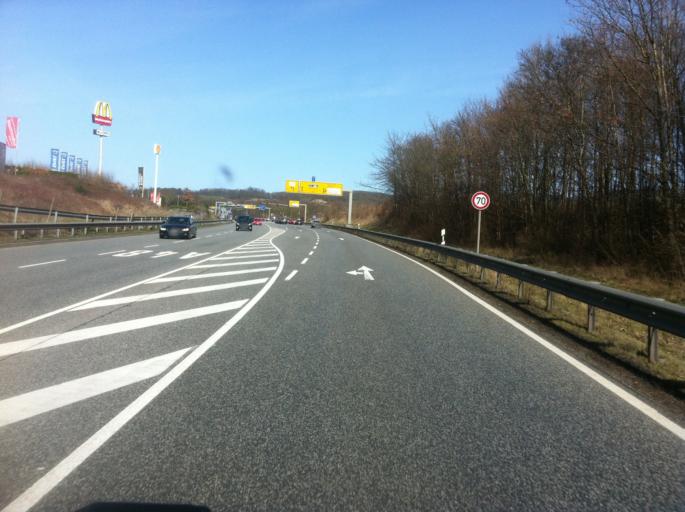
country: DE
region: Rheinland-Pfalz
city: Mendig
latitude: 50.3801
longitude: 7.2707
